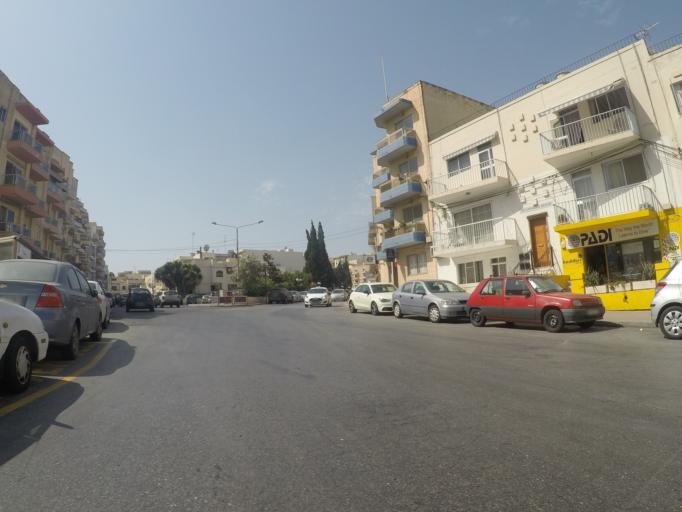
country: MT
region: Saint Paul's Bay
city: San Pawl il-Bahar
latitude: 35.9506
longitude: 14.4145
